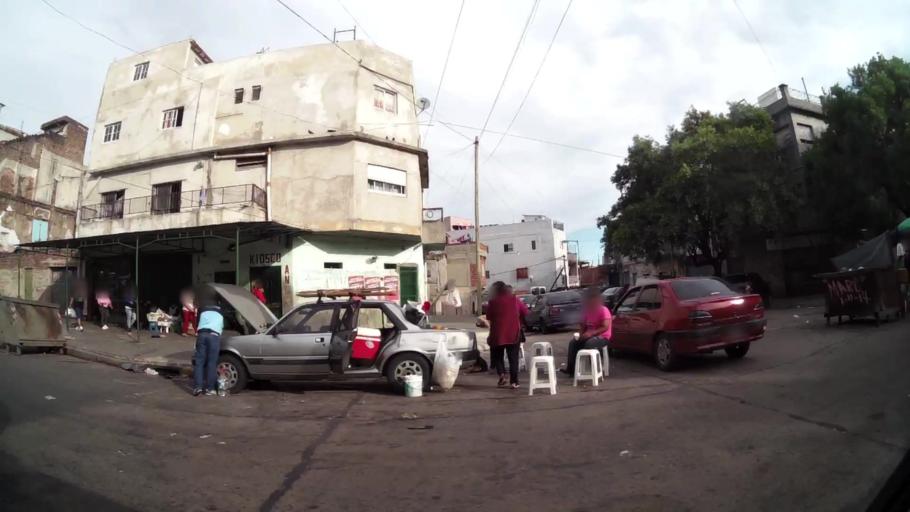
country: AR
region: Buenos Aires F.D.
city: Villa Lugano
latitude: -34.6437
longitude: -58.4452
